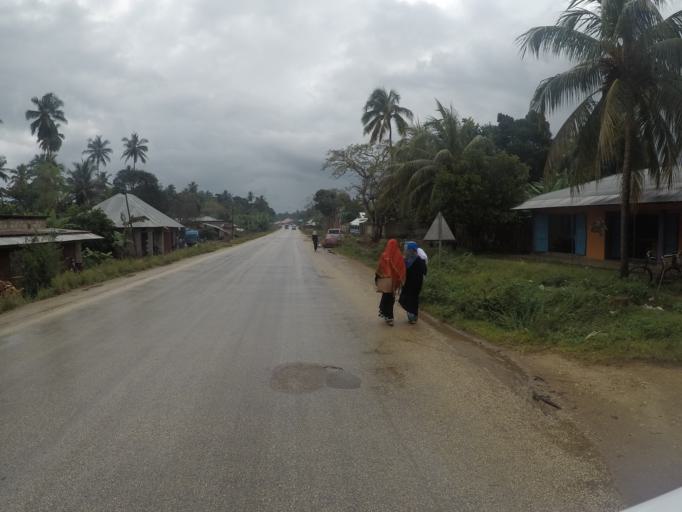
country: TZ
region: Zanzibar Central/South
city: Koani
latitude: -6.0515
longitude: 39.2255
